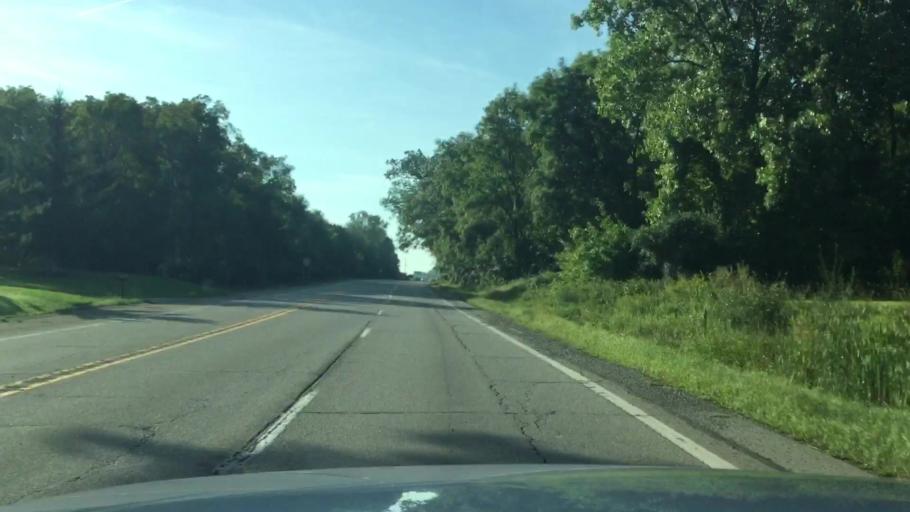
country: US
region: Michigan
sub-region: Lenawee County
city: Manitou Beach-Devils Lake
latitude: 42.0442
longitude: -84.3563
